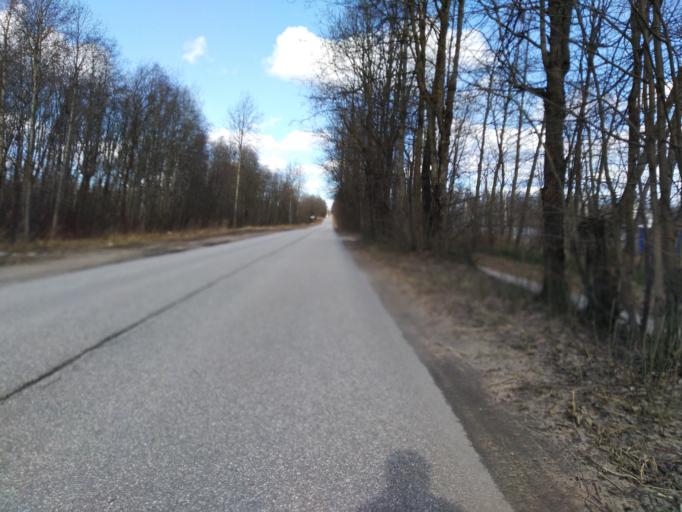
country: RU
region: Leningrad
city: Novoye Devyatkino
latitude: 60.0993
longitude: 30.4774
